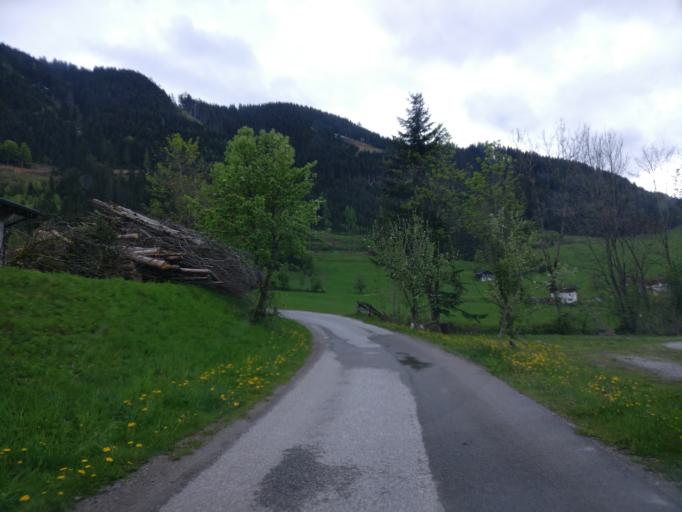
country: AT
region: Salzburg
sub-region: Politischer Bezirk Sankt Johann im Pongau
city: Werfenweng
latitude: 47.4585
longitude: 13.2741
